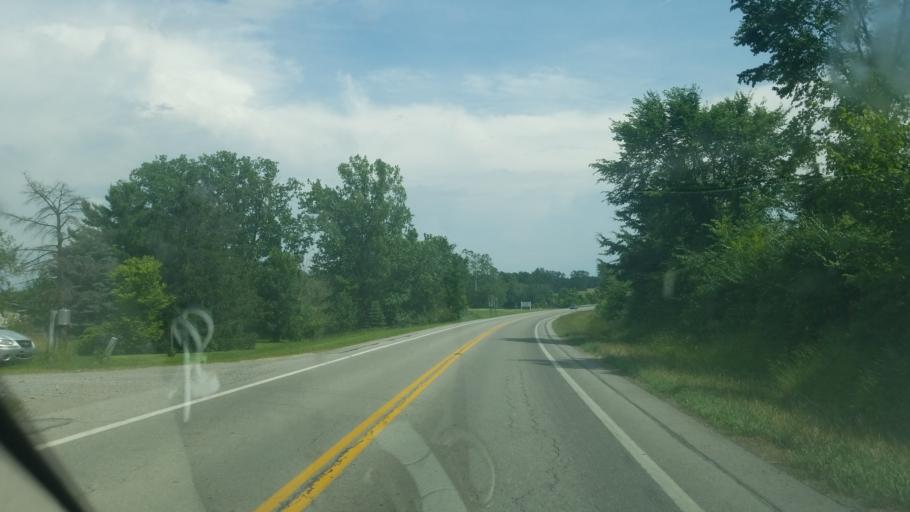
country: US
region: Ohio
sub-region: Logan County
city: Northwood
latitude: 40.4716
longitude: -83.7337
